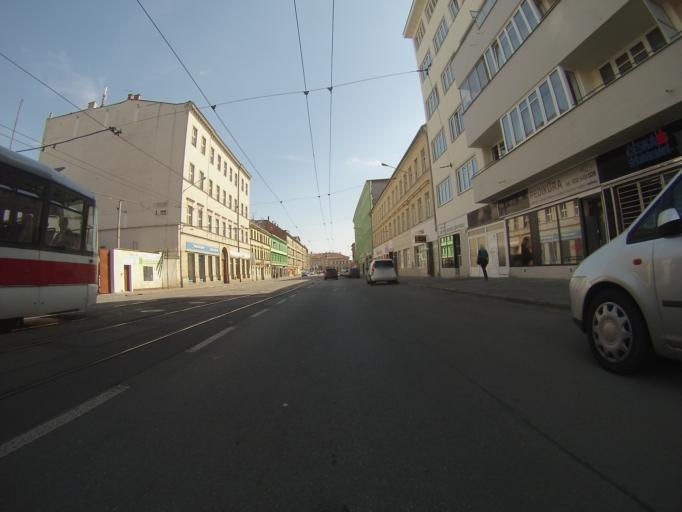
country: CZ
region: South Moravian
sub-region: Mesto Brno
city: Brno
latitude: 49.2017
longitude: 16.6261
